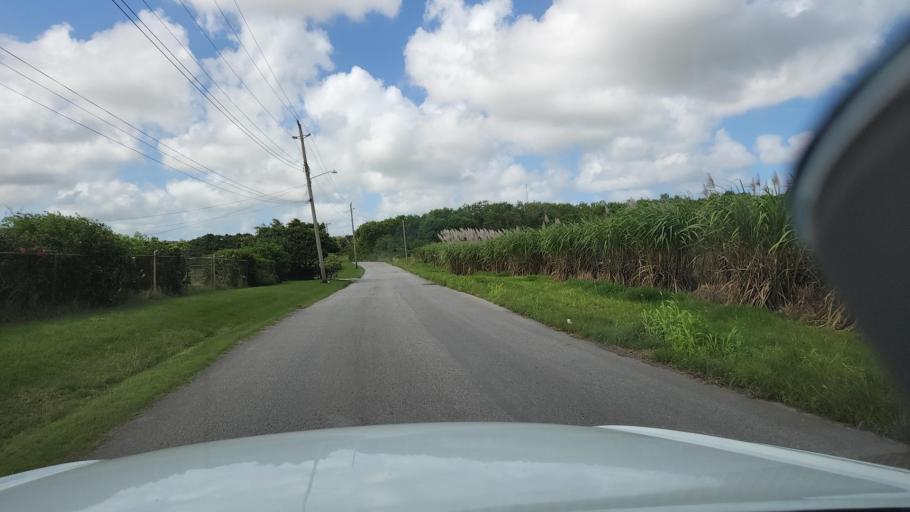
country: BB
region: Saint Philip
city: Crane
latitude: 13.1404
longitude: -59.4752
